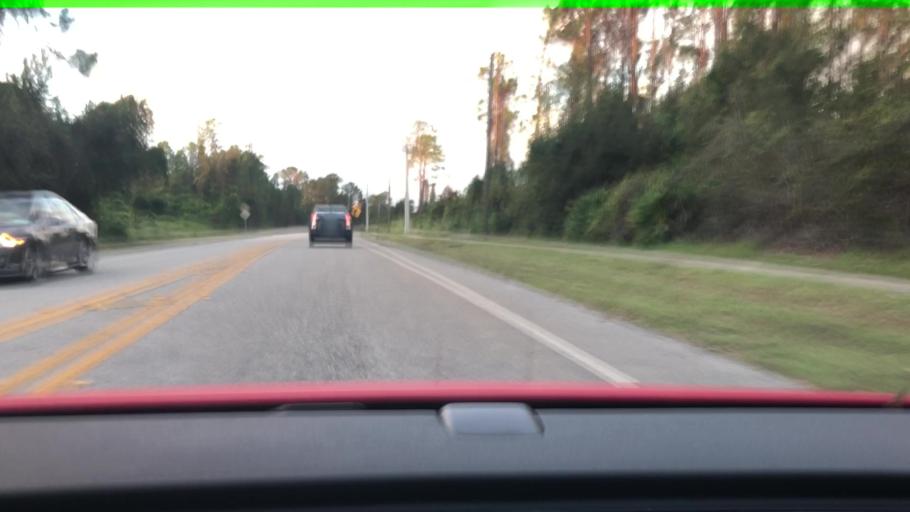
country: US
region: Florida
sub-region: Volusia County
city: South Daytona
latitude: 29.1527
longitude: -81.0229
